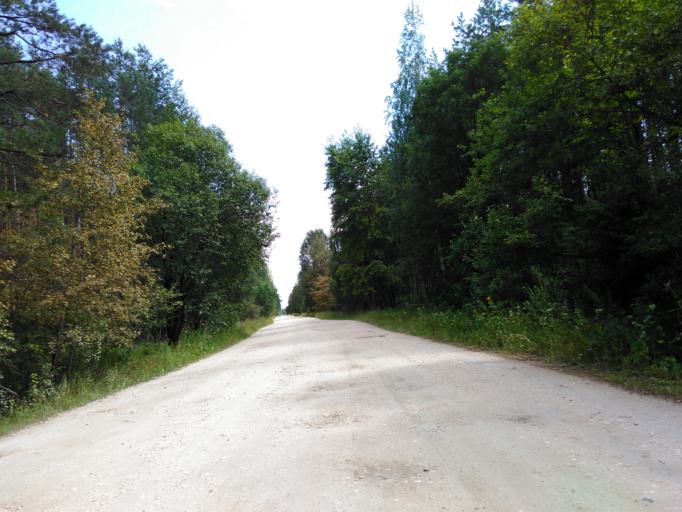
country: RU
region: Vladimir
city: Krasnyy Oktyabr'
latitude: 56.0050
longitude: 38.8368
